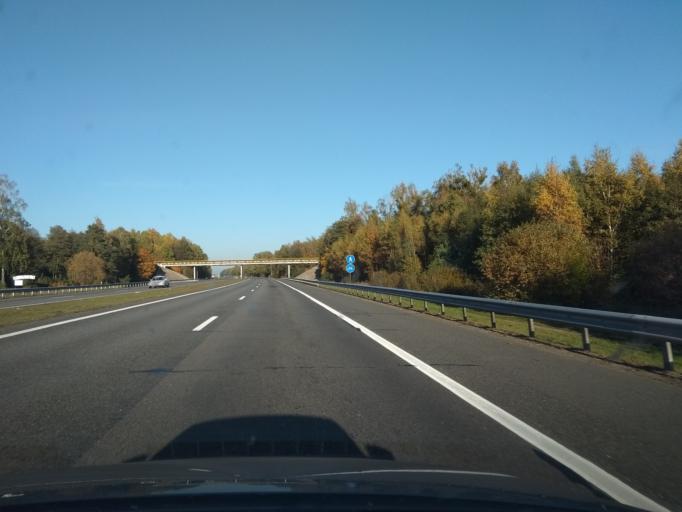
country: BY
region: Brest
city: Ivatsevichy
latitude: 52.6763
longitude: 25.3203
